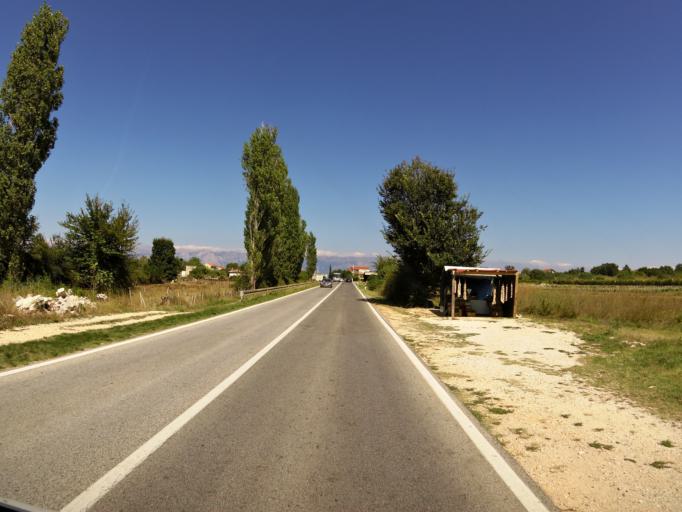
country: HR
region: Zadarska
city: Policnik
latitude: 44.1848
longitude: 15.3949
